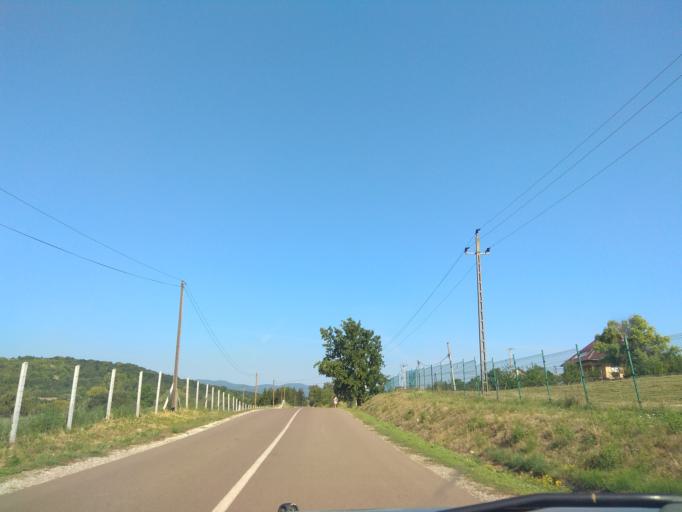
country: HU
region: Borsod-Abauj-Zemplen
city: Nyekladhaza
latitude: 47.9770
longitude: 20.7917
